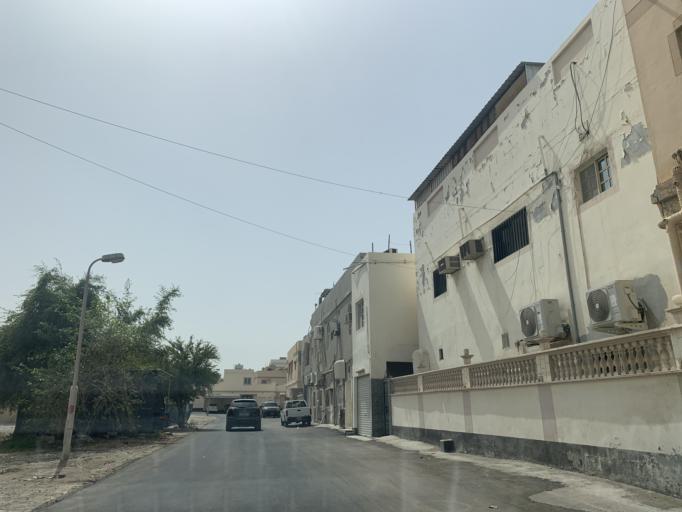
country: BH
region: Northern
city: Madinat `Isa
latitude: 26.1554
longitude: 50.5180
